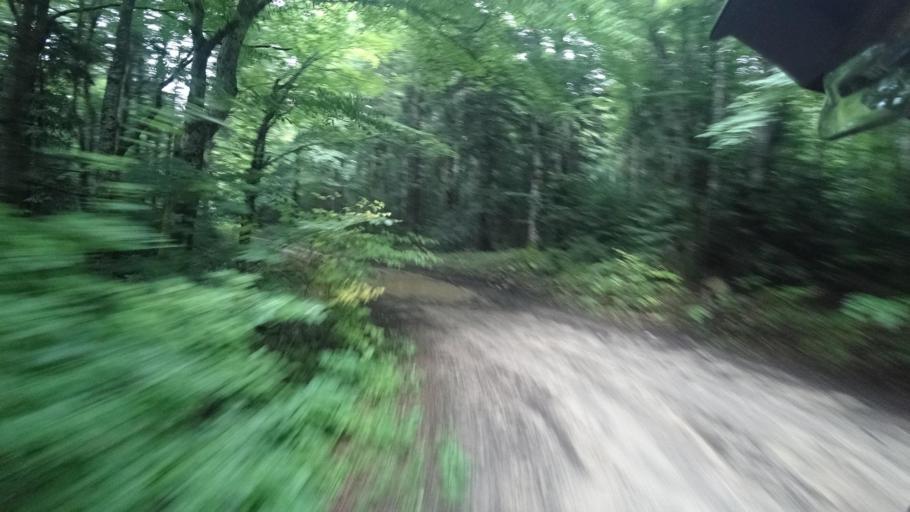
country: HR
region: Licko-Senjska
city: Jezerce
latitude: 44.7992
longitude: 15.6456
